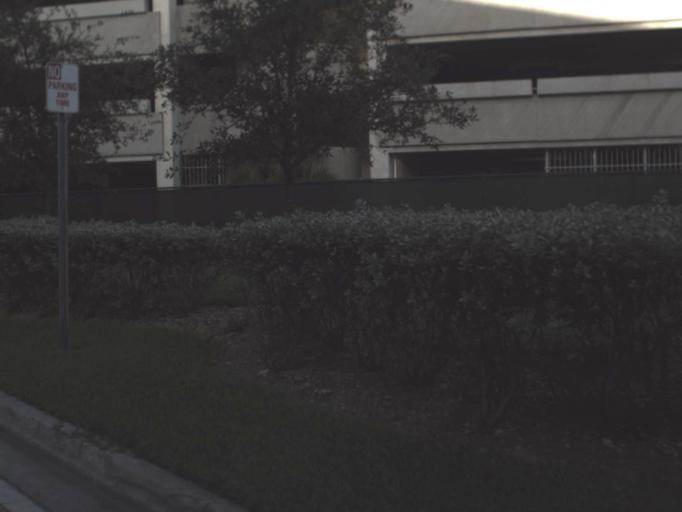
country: US
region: Florida
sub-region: Miami-Dade County
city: South Miami
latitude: 25.7049
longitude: -80.2904
